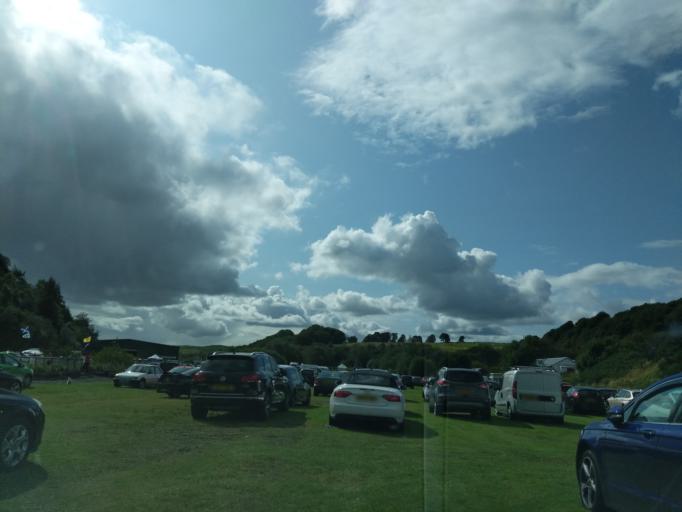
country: GB
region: Scotland
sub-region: Fife
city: Townhill
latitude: 56.1128
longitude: -3.4579
